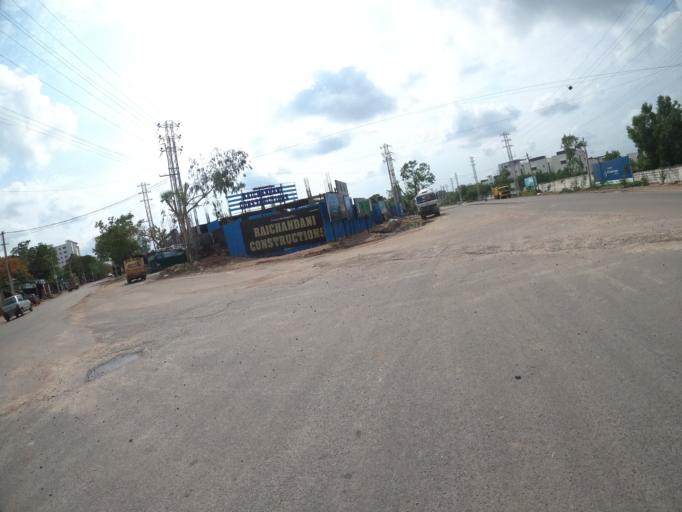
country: IN
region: Telangana
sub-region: Medak
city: Serilingampalle
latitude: 17.3853
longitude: 78.3309
